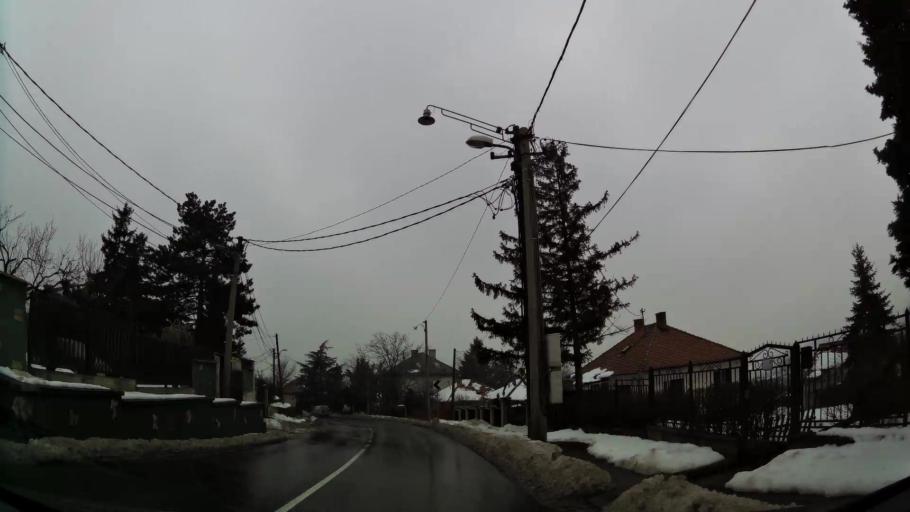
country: RS
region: Central Serbia
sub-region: Belgrade
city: Vozdovac
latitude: 44.7439
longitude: 20.4995
